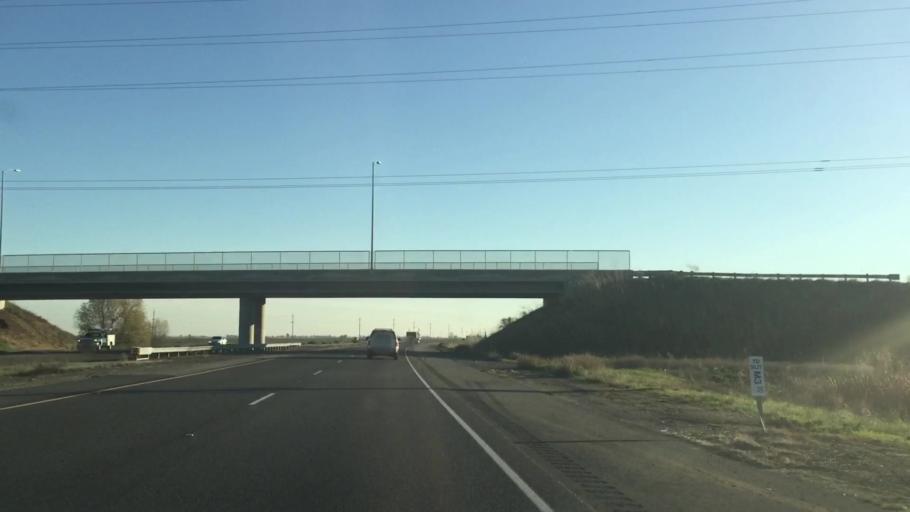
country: US
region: California
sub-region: Yuba County
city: Plumas Lake
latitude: 38.8959
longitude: -121.5445
